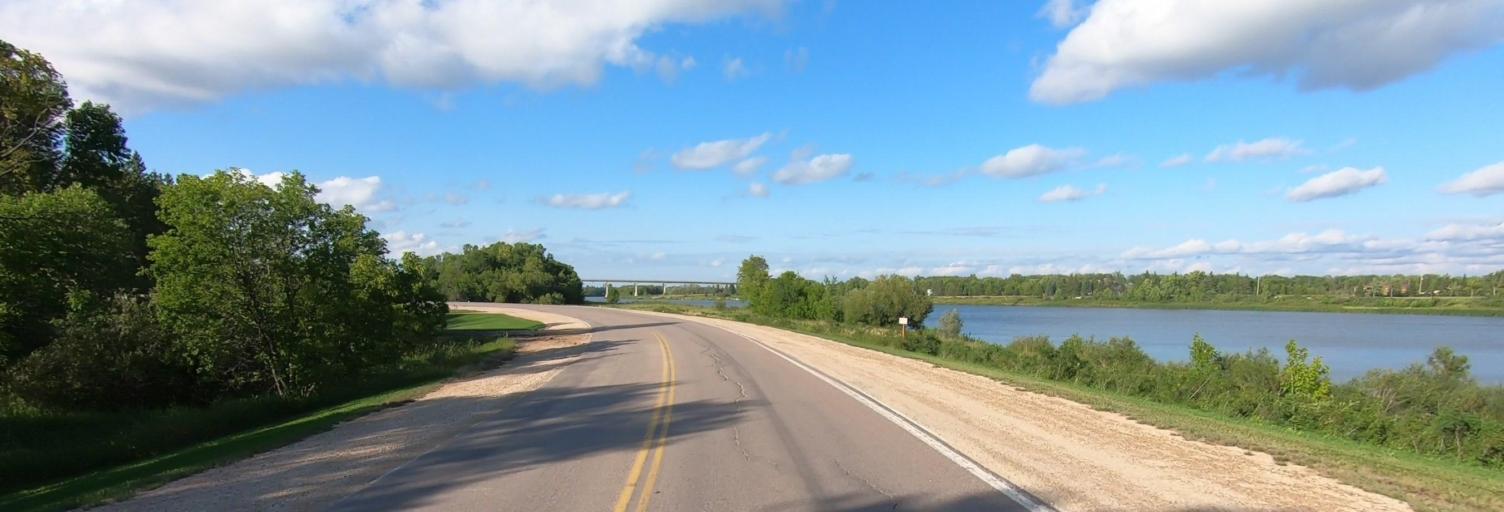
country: CA
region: Manitoba
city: Selkirk
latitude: 50.1828
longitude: -96.8445
